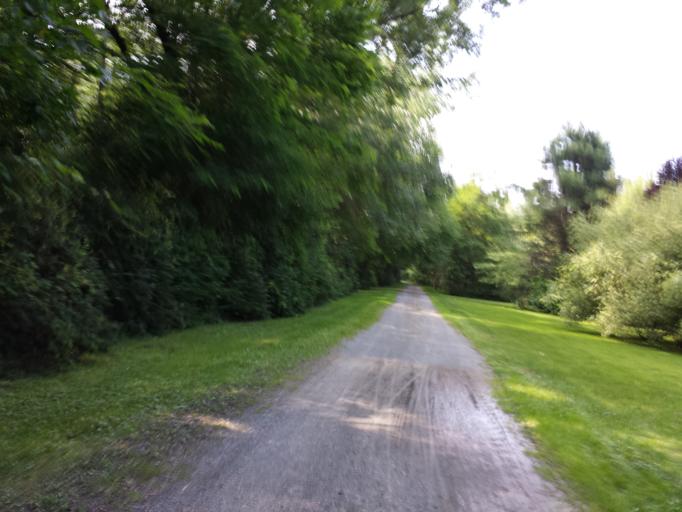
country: US
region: New York
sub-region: Saratoga County
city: Country Knolls
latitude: 42.9232
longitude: -73.7880
